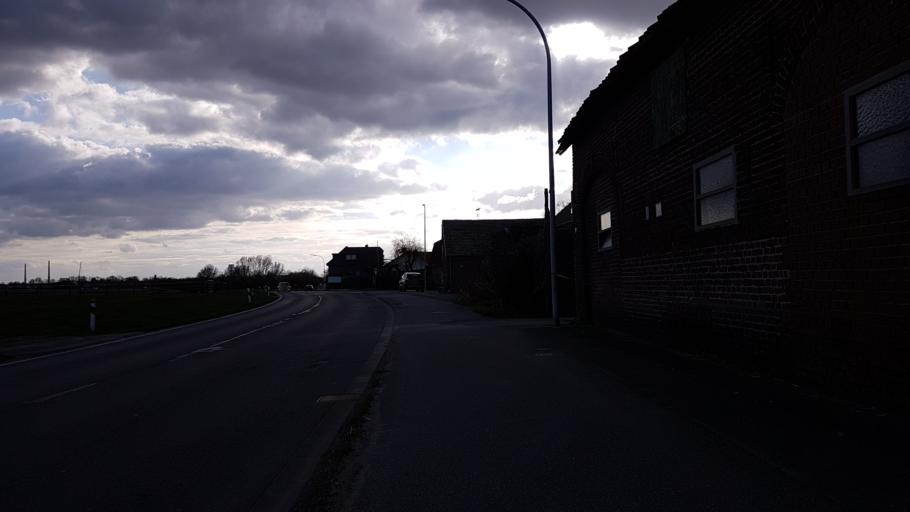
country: DE
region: North Rhine-Westphalia
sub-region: Regierungsbezirk Dusseldorf
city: Bruggen
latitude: 51.2234
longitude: 6.1991
